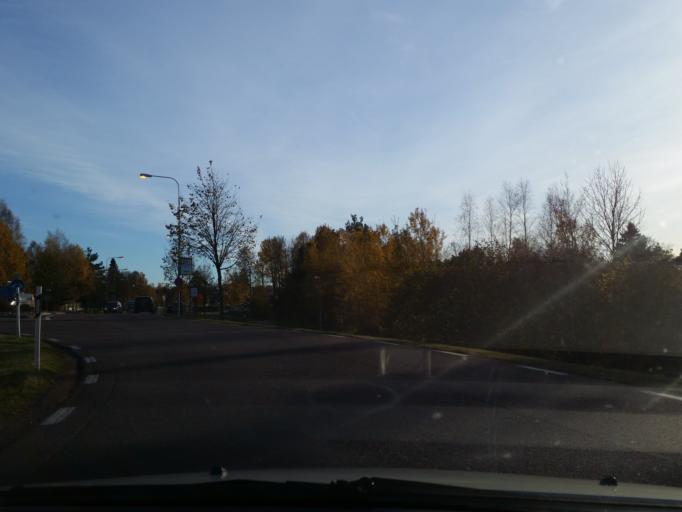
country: AX
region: Mariehamns stad
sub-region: Mariehamn
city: Mariehamn
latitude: 60.1136
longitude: 19.9288
